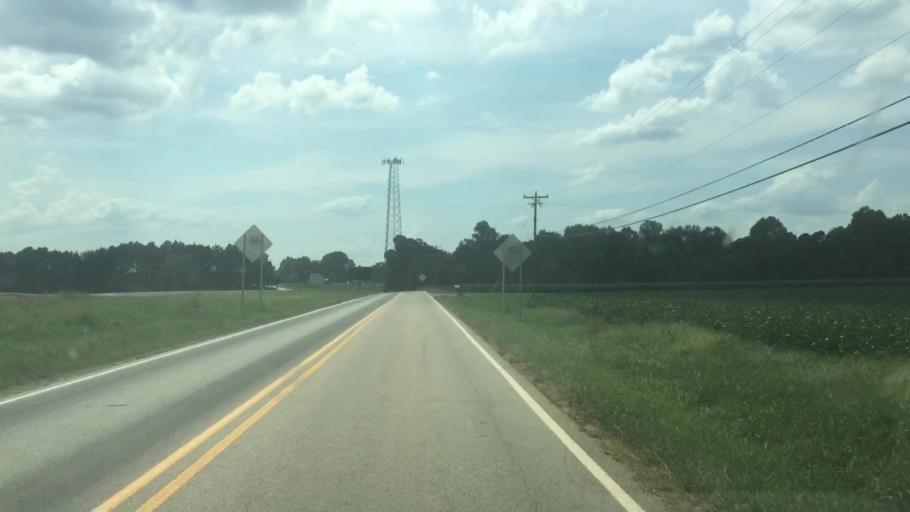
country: US
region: North Carolina
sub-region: Rowan County
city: Enochville
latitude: 35.6344
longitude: -80.6717
